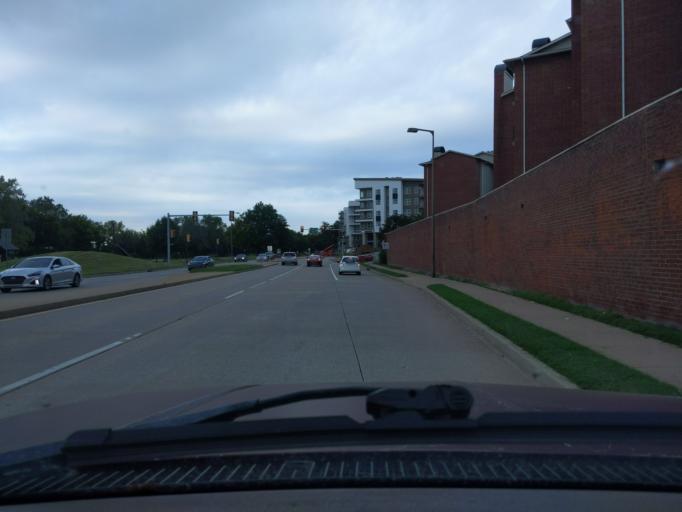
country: US
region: Oklahoma
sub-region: Tulsa County
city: Tulsa
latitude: 36.1351
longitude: -95.9918
